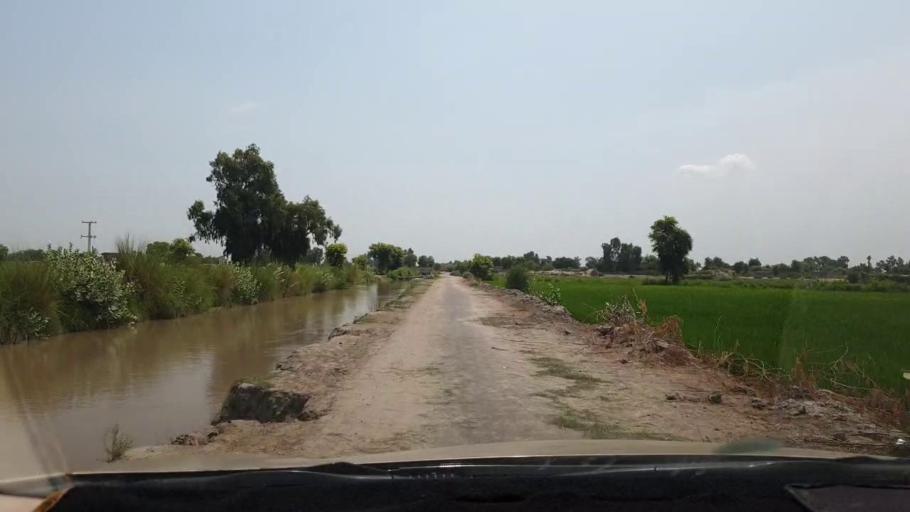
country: PK
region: Sindh
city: Naudero
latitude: 27.6587
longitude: 68.3292
